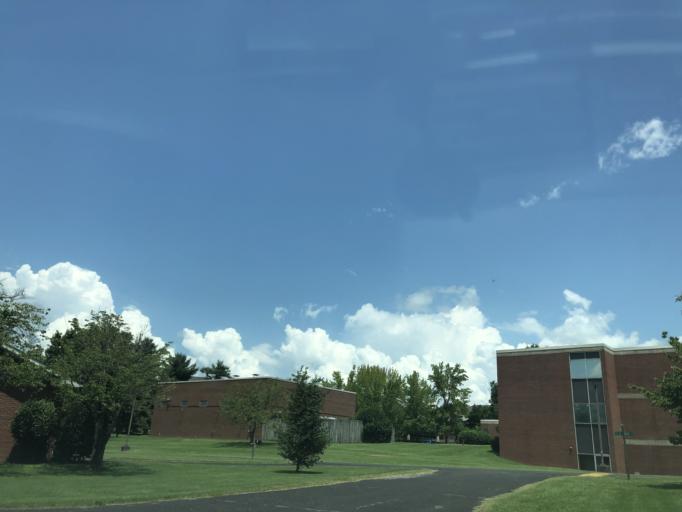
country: US
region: Tennessee
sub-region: Davidson County
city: Lakewood
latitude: 36.2050
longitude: -86.6111
